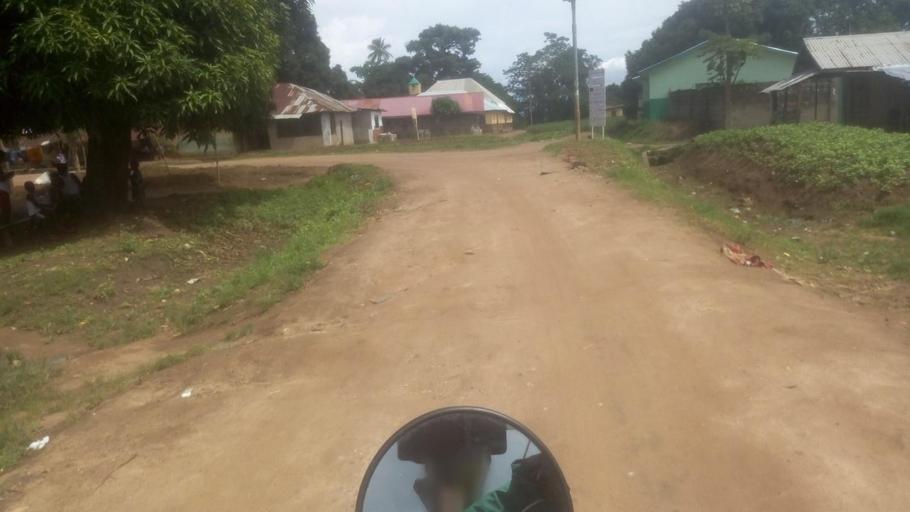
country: SL
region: Northern Province
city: Tintafor
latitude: 8.6399
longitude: -13.2269
